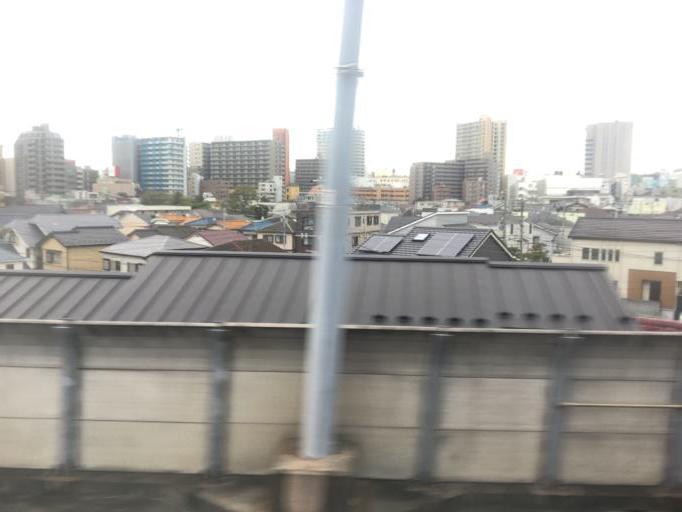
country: JP
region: Chiba
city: Funabashi
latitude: 35.6994
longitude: 139.9917
